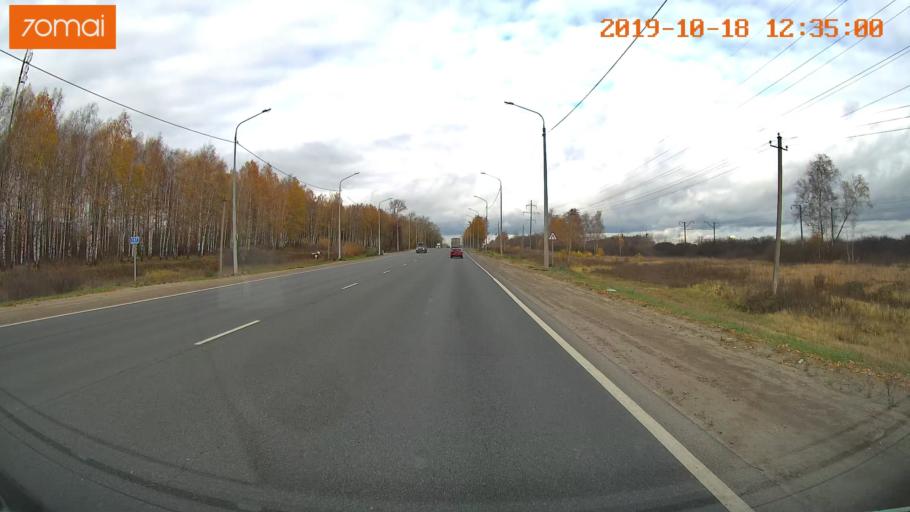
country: RU
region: Rjazan
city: Ryazan'
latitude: 54.6199
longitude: 39.6364
